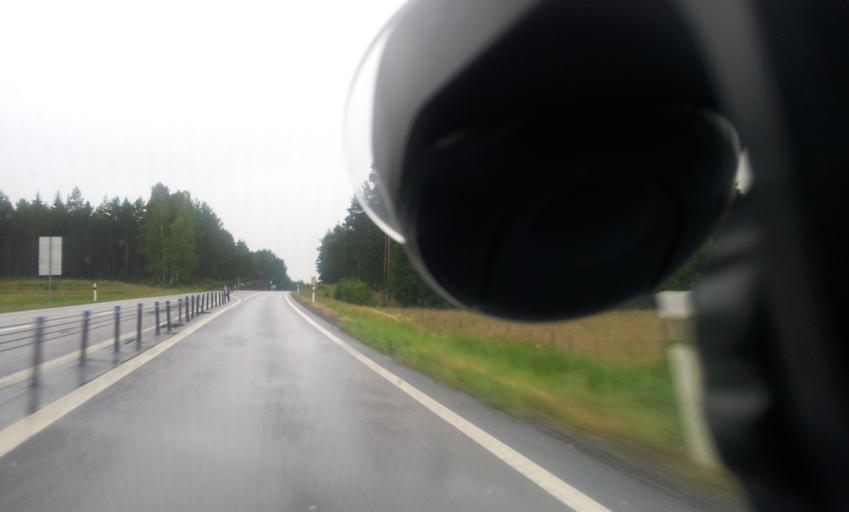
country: SE
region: OEstergoetland
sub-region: Valdemarsviks Kommun
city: Valdemarsvik
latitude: 58.1253
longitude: 16.5335
